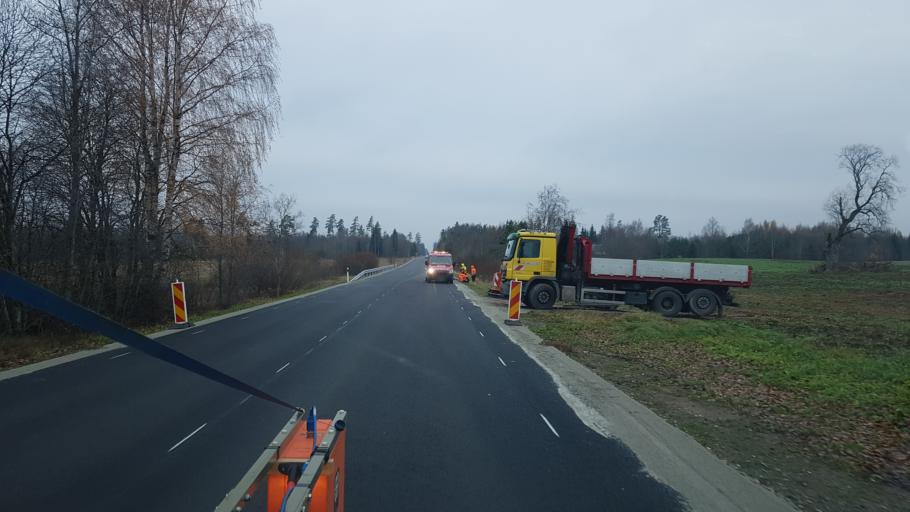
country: EE
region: Paernumaa
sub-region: Vaendra vald (alev)
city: Vandra
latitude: 58.8240
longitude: 25.1291
